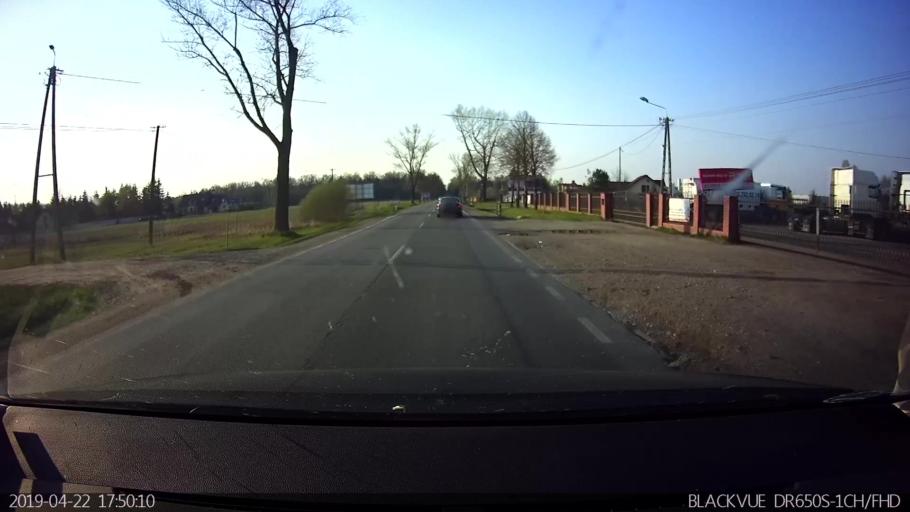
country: PL
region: Masovian Voivodeship
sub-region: Powiat wegrowski
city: Wegrow
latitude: 52.4215
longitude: 22.0039
